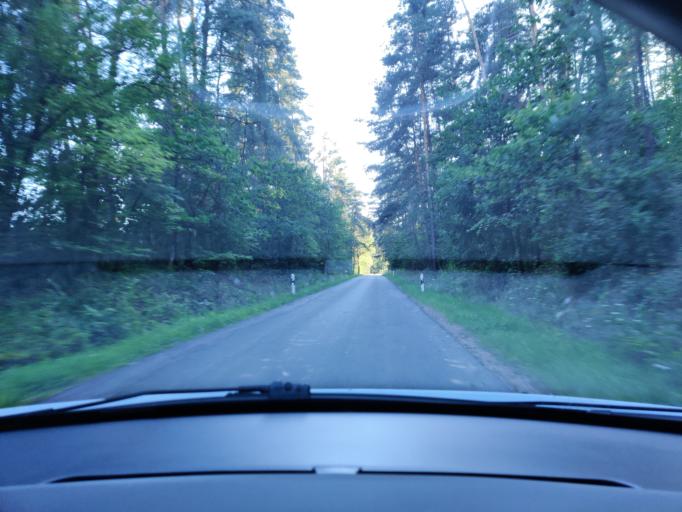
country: DE
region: Bavaria
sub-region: Upper Palatinate
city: Nabburg
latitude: 49.4277
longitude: 12.1655
